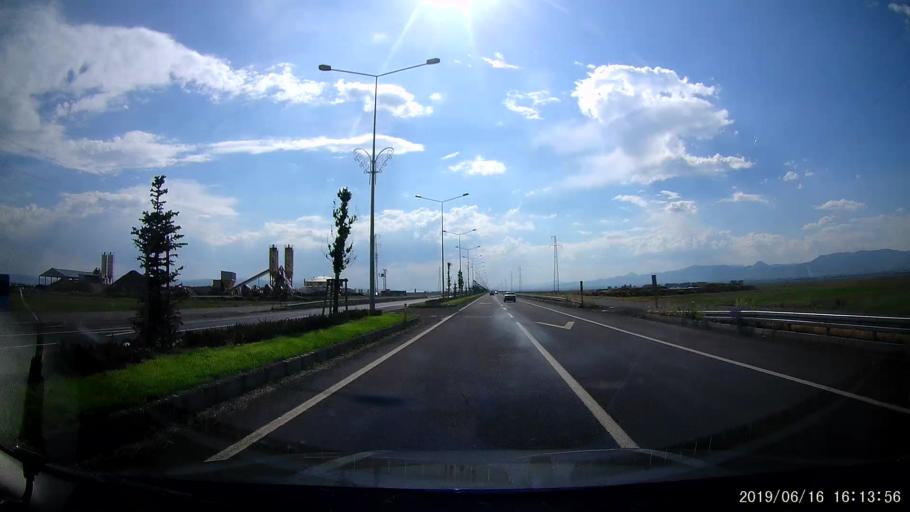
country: TR
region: Erzurum
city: Erzurum
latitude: 39.9601
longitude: 41.2614
